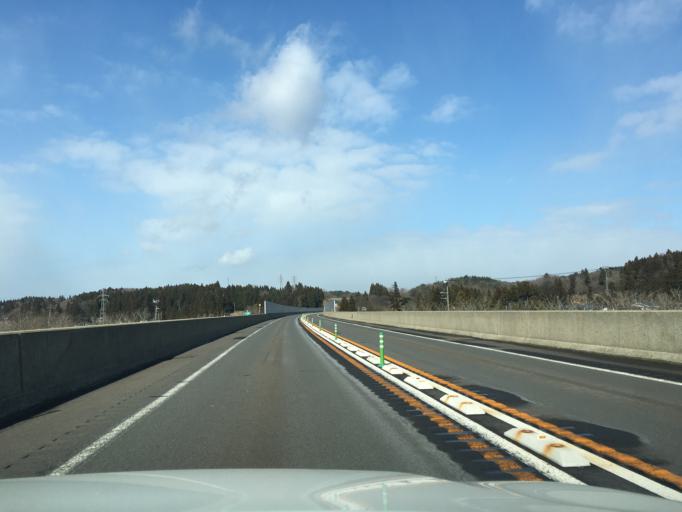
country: JP
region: Akita
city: Akita
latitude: 39.7541
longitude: 140.1407
